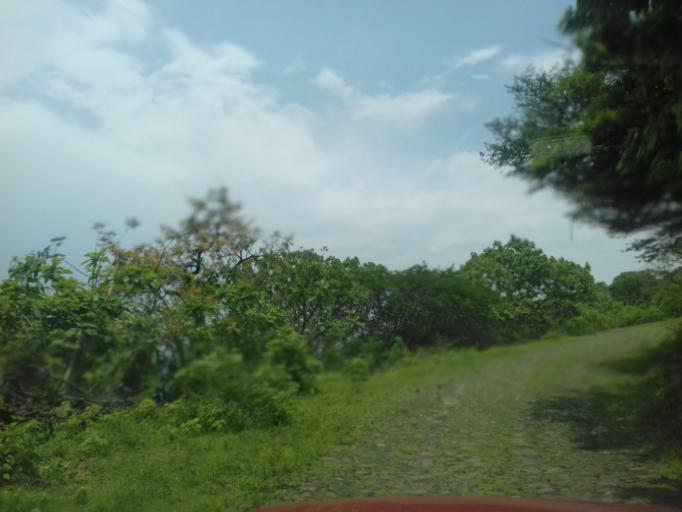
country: MX
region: Nayarit
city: Jala
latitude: 21.1076
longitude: -104.4896
